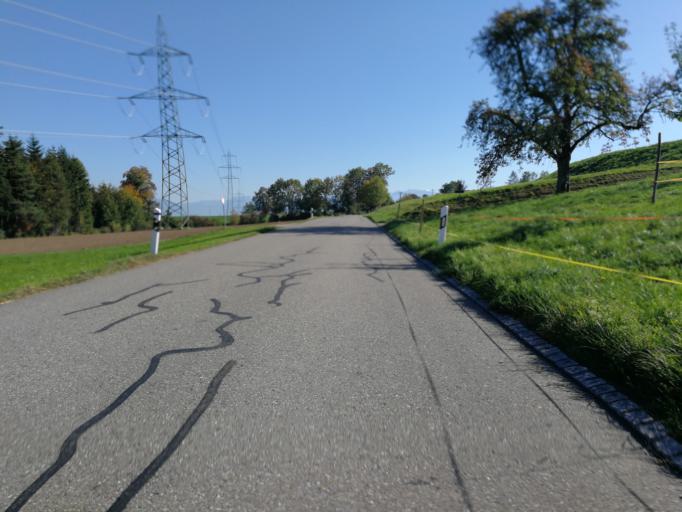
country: CH
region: Zurich
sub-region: Bezirk Uster
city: Hinteregg
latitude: 47.3177
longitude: 8.6736
